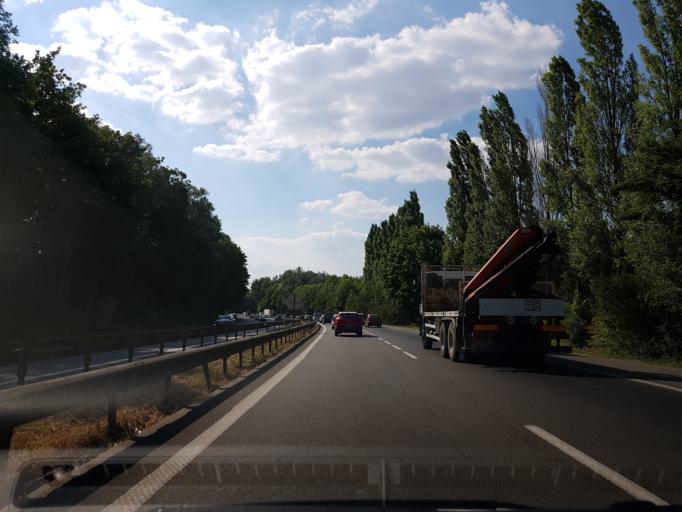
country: FR
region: Nord-Pas-de-Calais
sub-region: Departement du Pas-de-Calais
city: Courcelles-les-Lens
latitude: 50.4225
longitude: 3.0267
